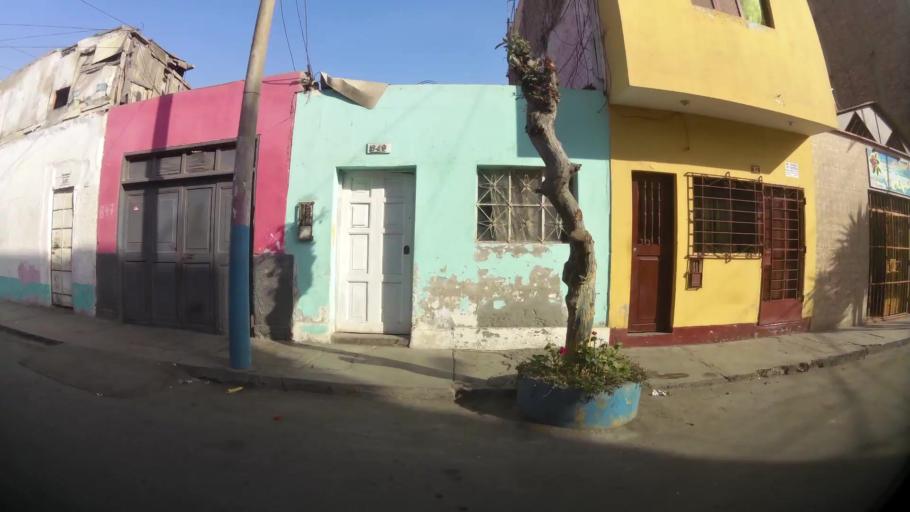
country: PE
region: Lima
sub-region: Huaura
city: Huacho
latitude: -11.1101
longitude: -77.6124
